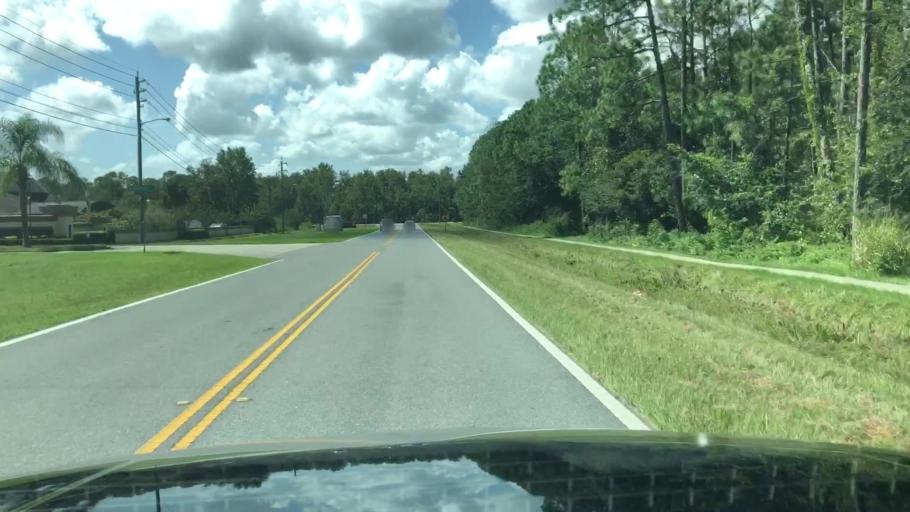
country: US
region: Florida
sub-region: Osceola County
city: Celebration
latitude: 28.3170
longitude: -81.4847
